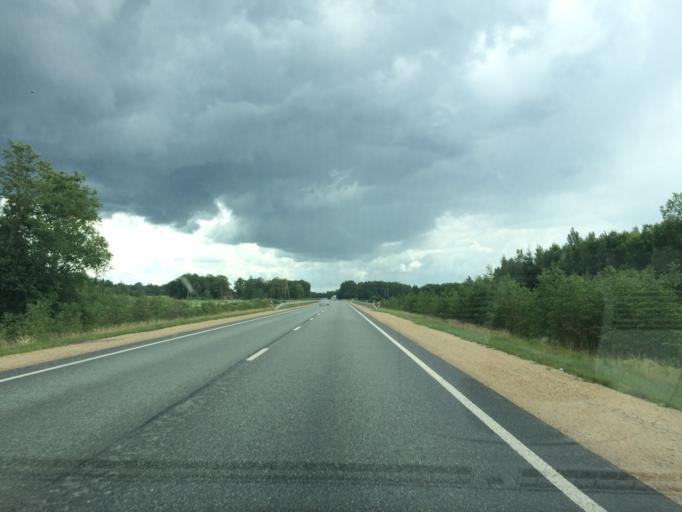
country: LV
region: Skriveri
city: Skriveri
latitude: 56.7144
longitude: 25.2120
